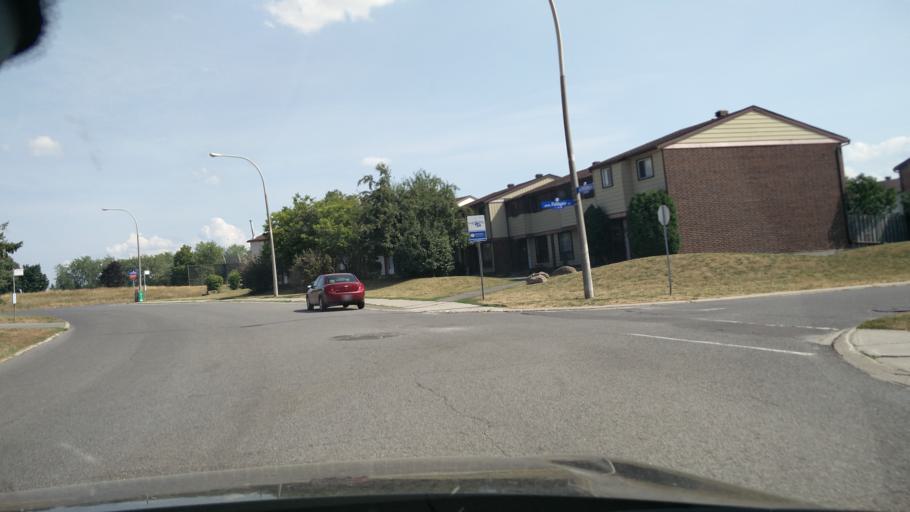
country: CA
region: Ontario
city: Bells Corners
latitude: 45.2880
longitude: -75.7513
